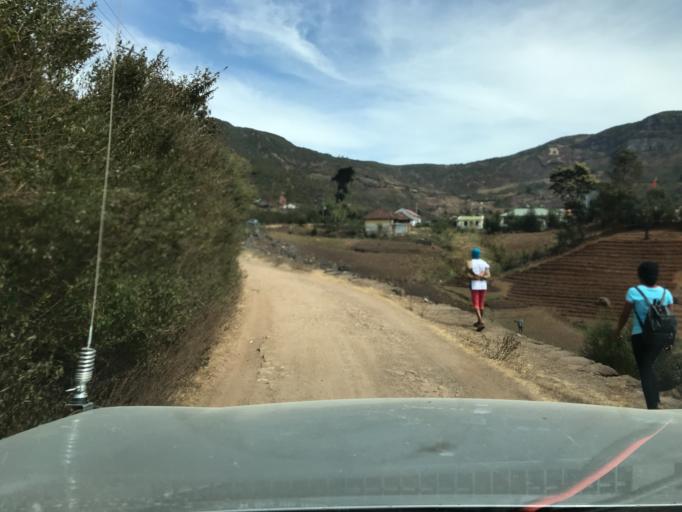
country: TL
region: Ainaro
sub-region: Ainaro
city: Ainaro
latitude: -8.8956
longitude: 125.5198
